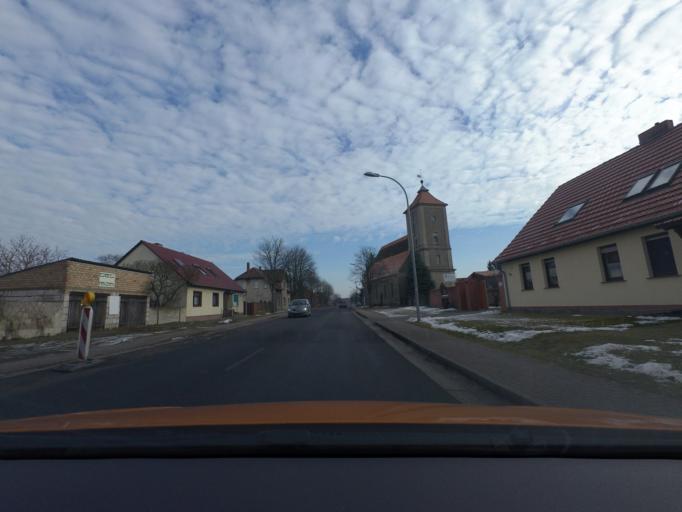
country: DE
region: Brandenburg
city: Ruthnick
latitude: 52.9010
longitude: 13.0453
